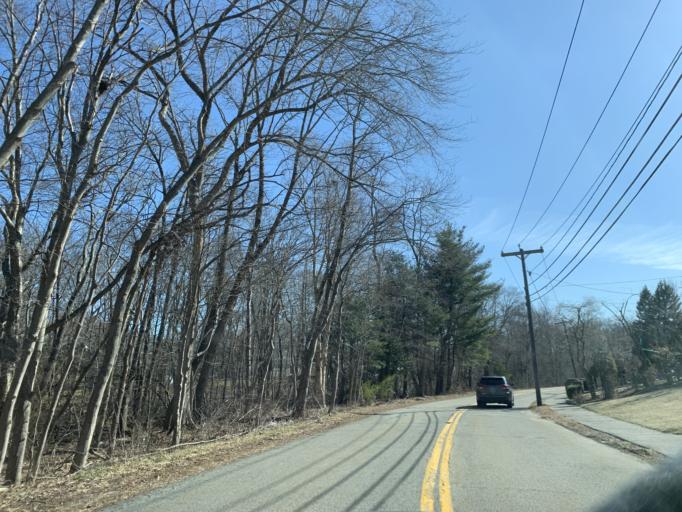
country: US
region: Massachusetts
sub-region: Norfolk County
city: Westwood
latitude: 42.1923
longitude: -71.2230
